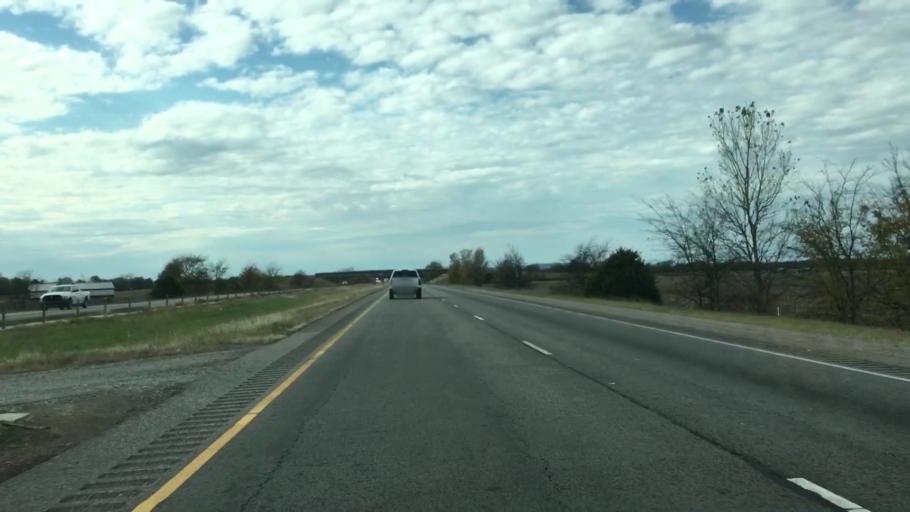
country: US
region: Arkansas
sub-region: Conway County
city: Morrilton
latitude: 35.1897
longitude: -92.7834
